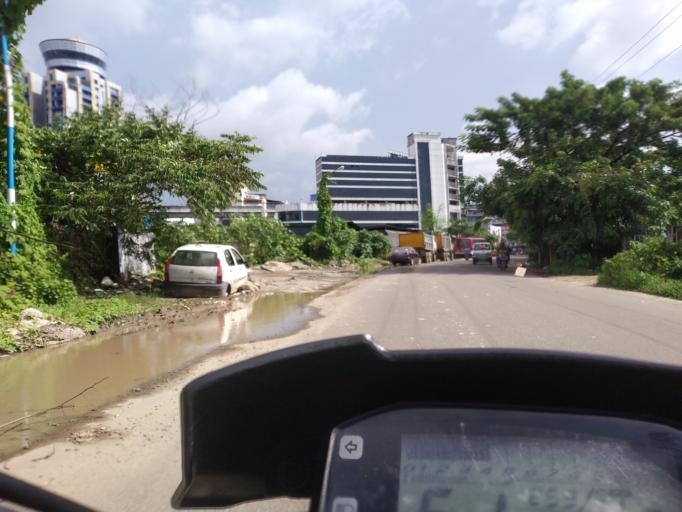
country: IN
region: Kerala
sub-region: Ernakulam
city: Cochin
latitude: 9.9940
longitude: 76.2891
